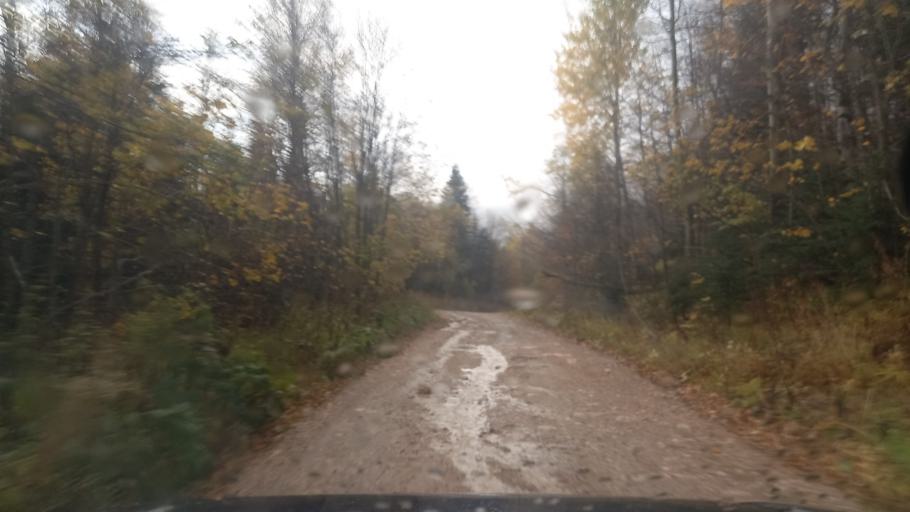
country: RU
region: Krasnodarskiy
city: Gornoye Loo
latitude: 44.0072
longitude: 39.8435
